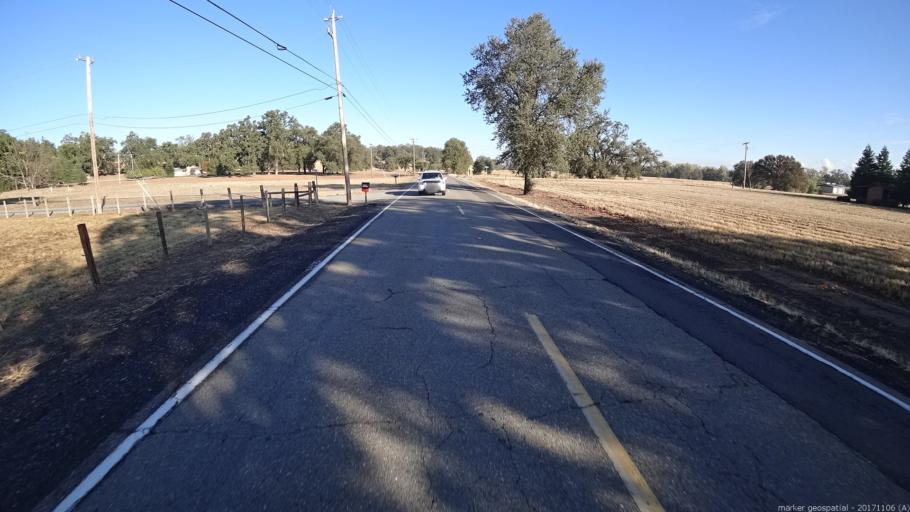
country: US
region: California
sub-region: Shasta County
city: Palo Cedro
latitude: 40.4939
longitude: -122.2387
